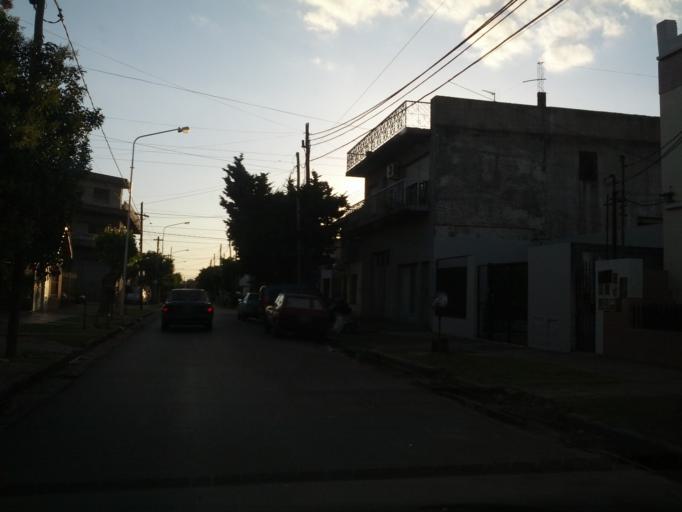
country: AR
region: Buenos Aires
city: San Justo
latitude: -34.6562
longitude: -58.5431
